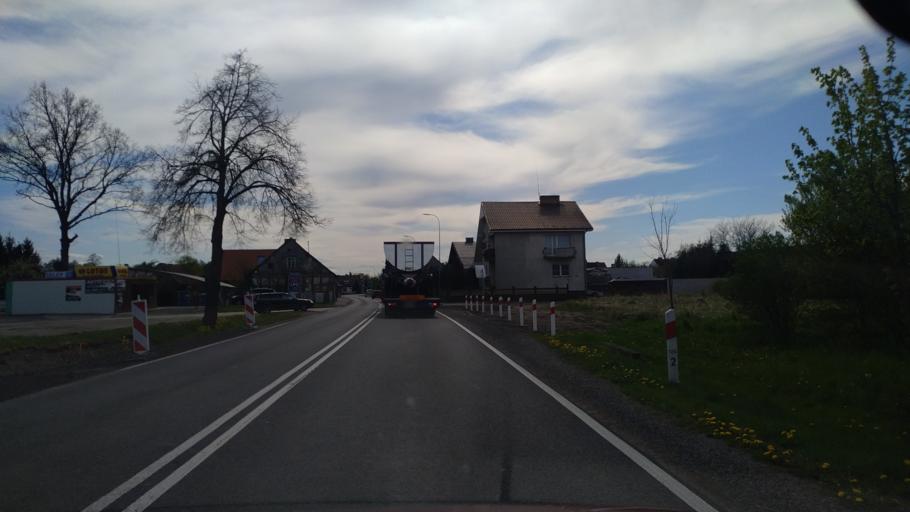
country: PL
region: West Pomeranian Voivodeship
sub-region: Powiat walecki
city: Miroslawiec
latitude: 53.3440
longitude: 16.0973
